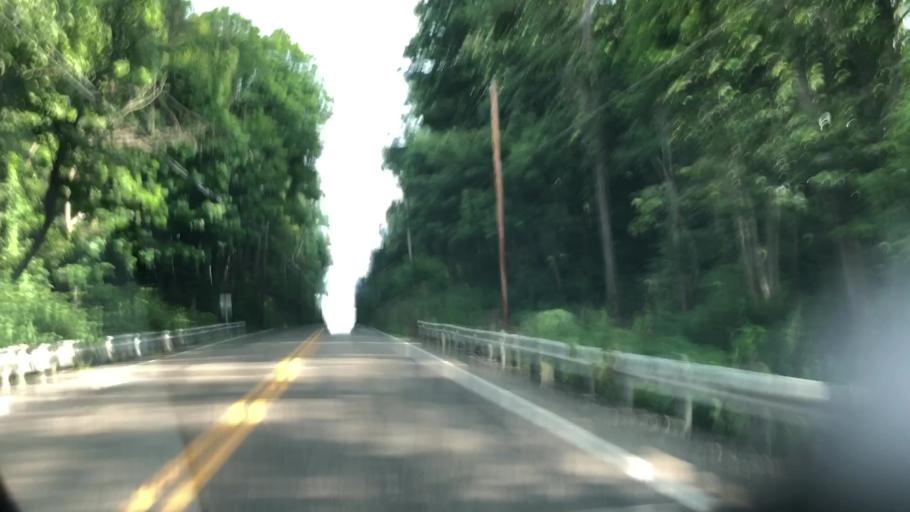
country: US
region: Ohio
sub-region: Summit County
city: Norton
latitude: 41.0698
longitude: -81.6395
